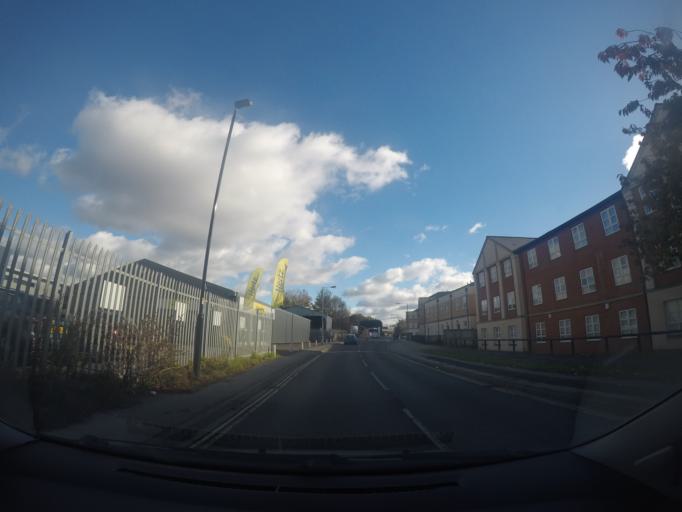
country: GB
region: England
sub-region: City of York
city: York
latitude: 53.9616
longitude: -1.1012
